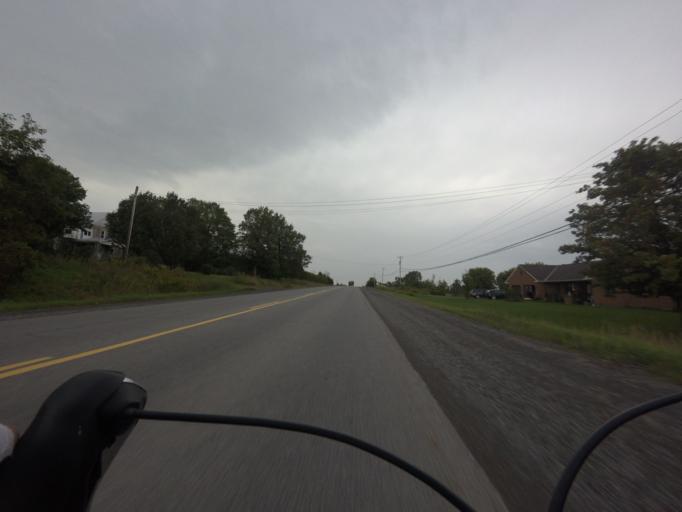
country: CA
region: Ontario
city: Bells Corners
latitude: 45.1673
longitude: -75.7126
